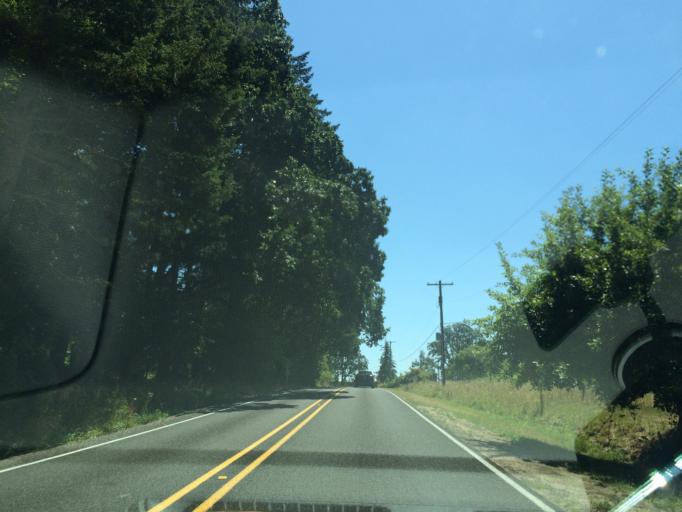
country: US
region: Oregon
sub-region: Clackamas County
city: Wilsonville
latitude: 45.2586
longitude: -122.8425
